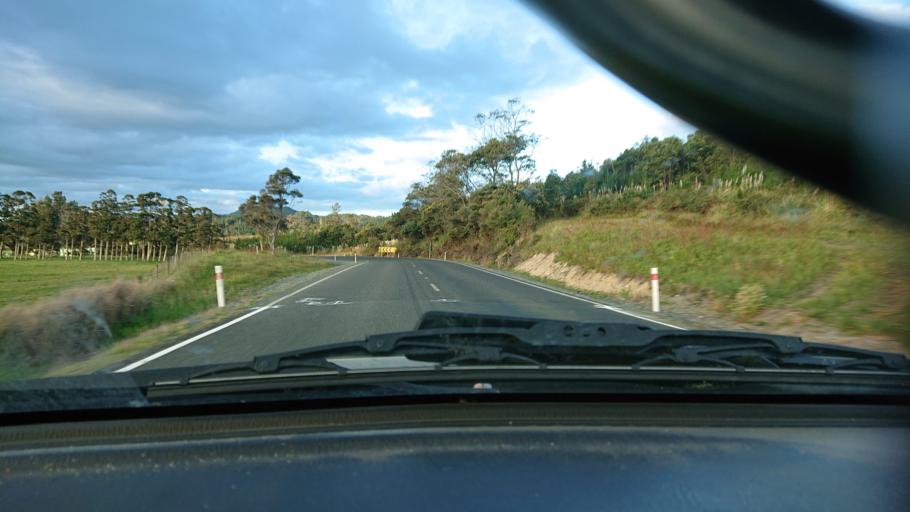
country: NZ
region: Auckland
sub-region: Auckland
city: Parakai
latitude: -36.5145
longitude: 174.4520
